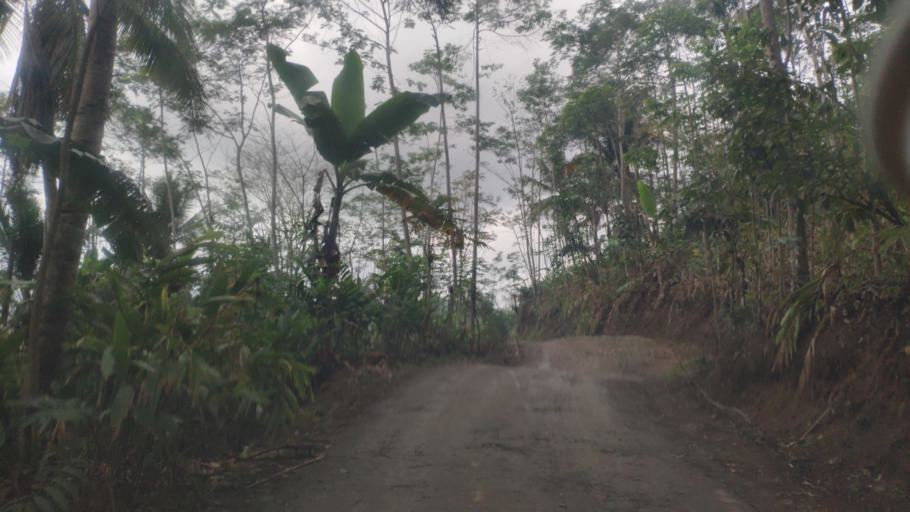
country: ID
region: Central Java
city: Purbalingga
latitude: -7.3081
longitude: 109.5820
